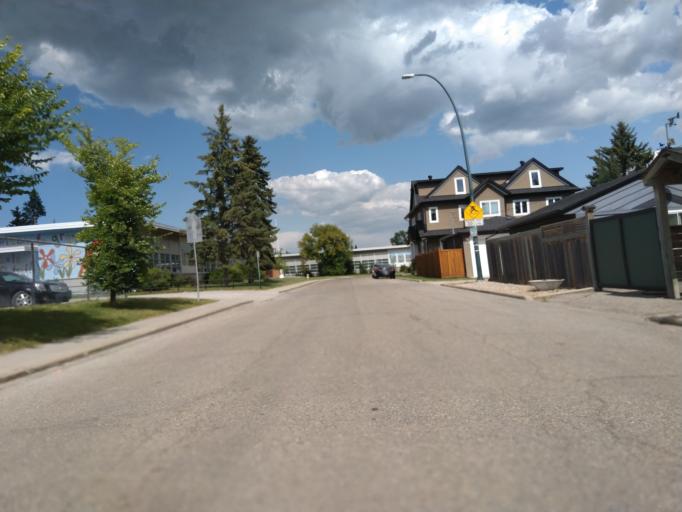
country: CA
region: Alberta
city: Calgary
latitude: 51.0806
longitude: -114.1175
